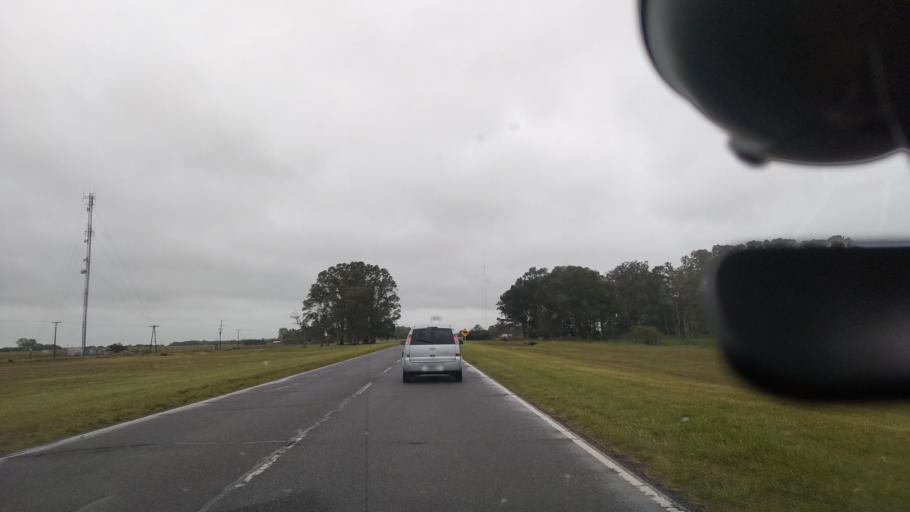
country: AR
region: Buenos Aires
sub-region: Partido de Castelli
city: Castelli
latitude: -35.9852
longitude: -57.4498
